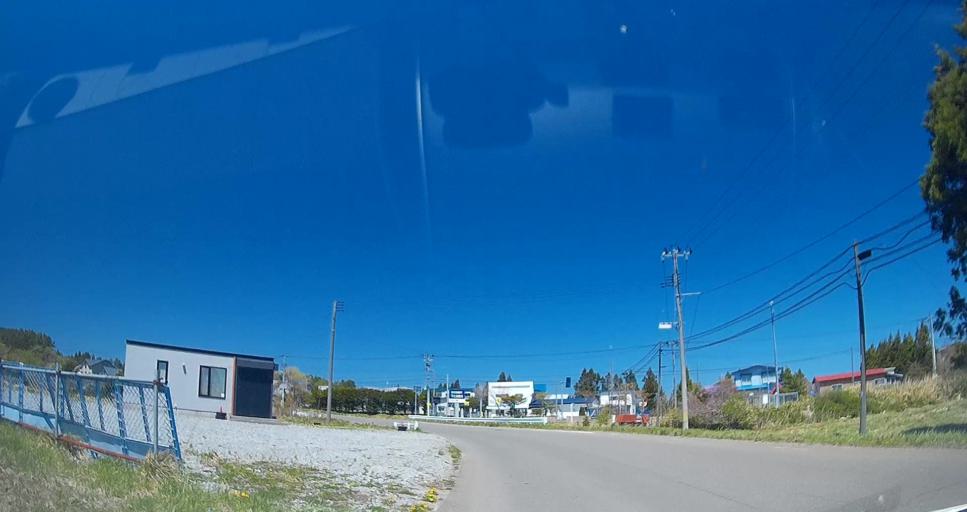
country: JP
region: Aomori
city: Mutsu
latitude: 41.2350
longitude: 141.3975
